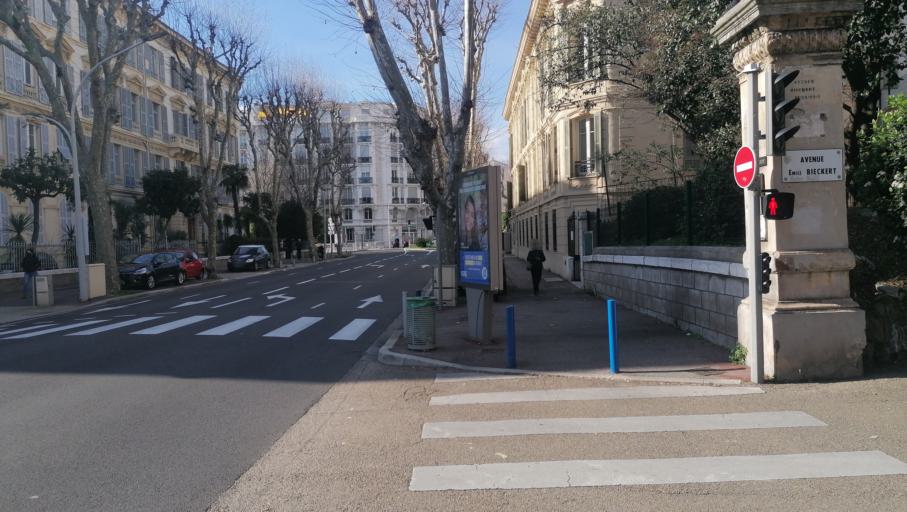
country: FR
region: Provence-Alpes-Cote d'Azur
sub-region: Departement des Alpes-Maritimes
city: Nice
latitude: 43.7040
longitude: 7.2744
